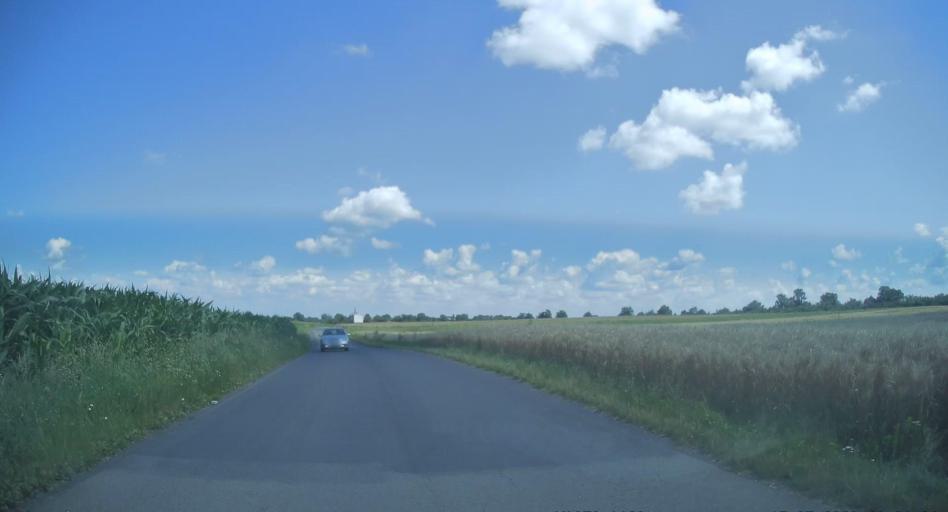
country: PL
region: Subcarpathian Voivodeship
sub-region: Powiat jaroslawski
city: Sosnica
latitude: 49.8535
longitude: 22.8787
